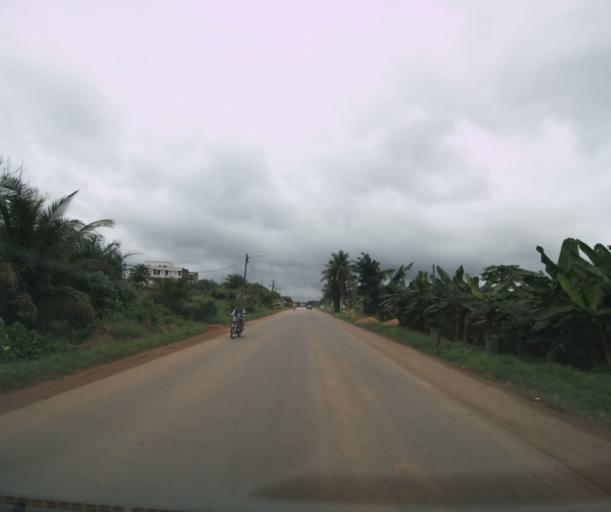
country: CM
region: Littoral
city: Edea
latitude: 3.7871
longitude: 10.1399
